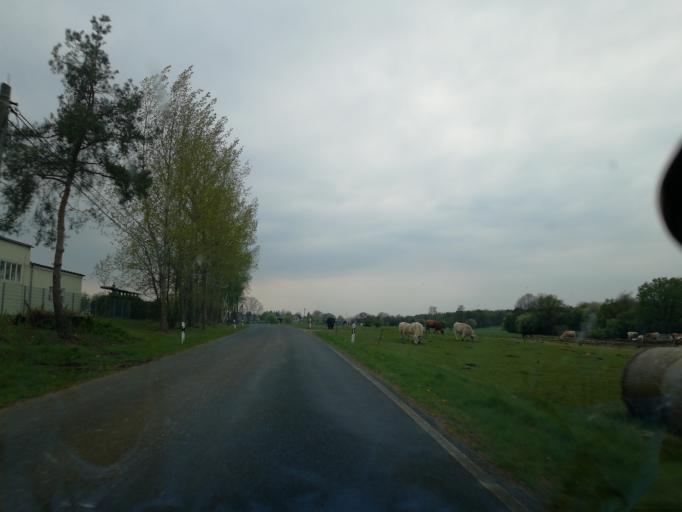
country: DE
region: Brandenburg
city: Lubbenau
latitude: 51.8217
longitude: 13.9096
